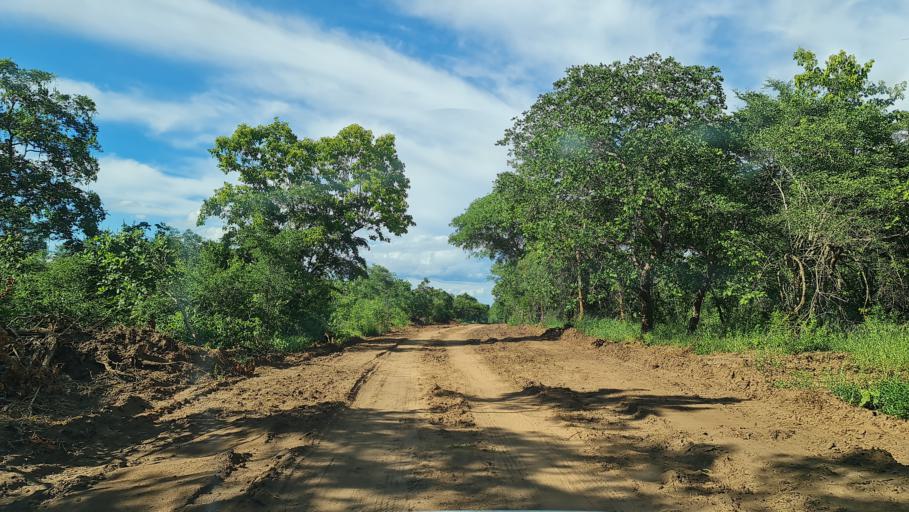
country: MZ
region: Nampula
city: Antonio Enes
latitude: -15.5149
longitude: 40.1306
